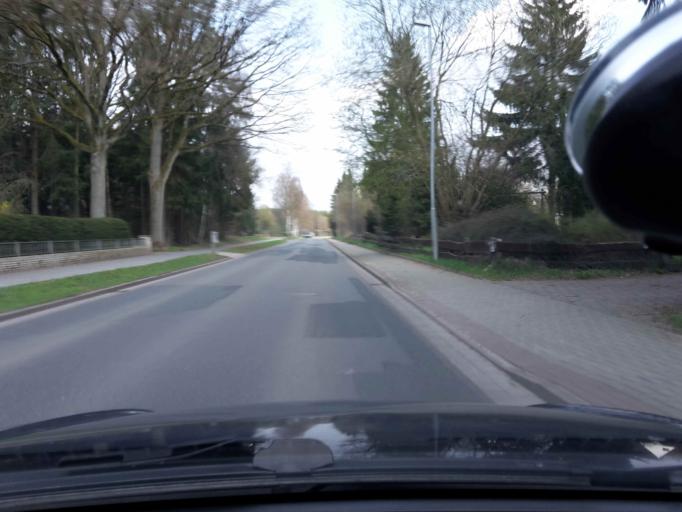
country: DE
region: Lower Saxony
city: Buchholz in der Nordheide
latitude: 53.2938
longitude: 9.8701
